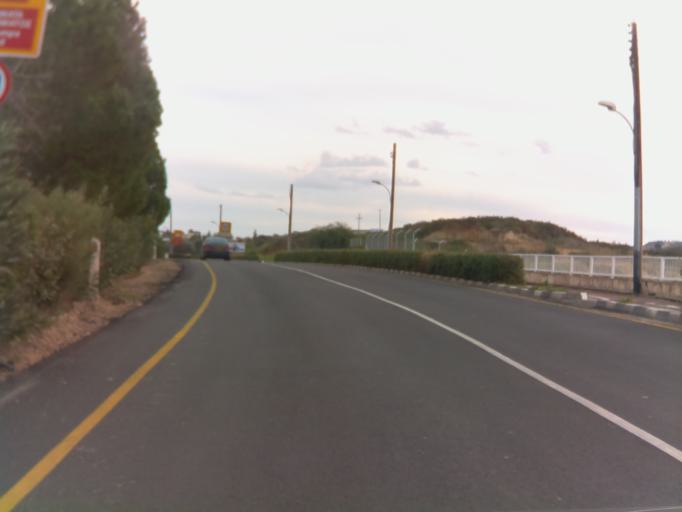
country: CY
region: Pafos
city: Polis
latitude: 35.0367
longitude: 32.4073
